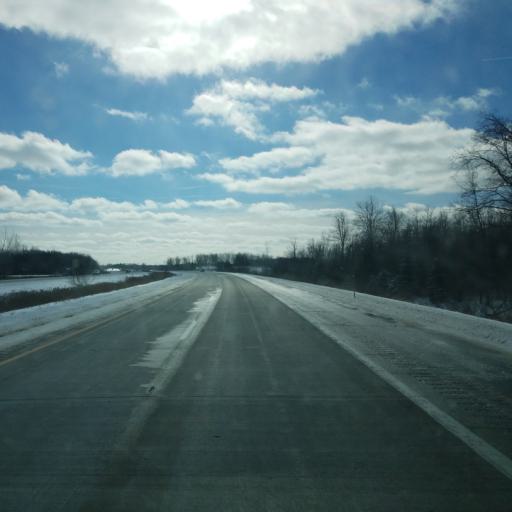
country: US
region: Michigan
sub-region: Clinton County
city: DeWitt
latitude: 42.8298
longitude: -84.5191
